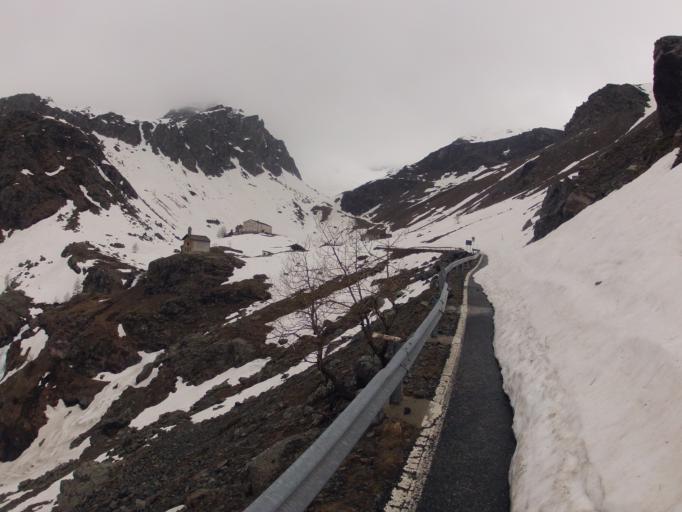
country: IT
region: Piedmont
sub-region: Provincia di Cuneo
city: Crissolo
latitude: 44.6999
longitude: 7.0997
